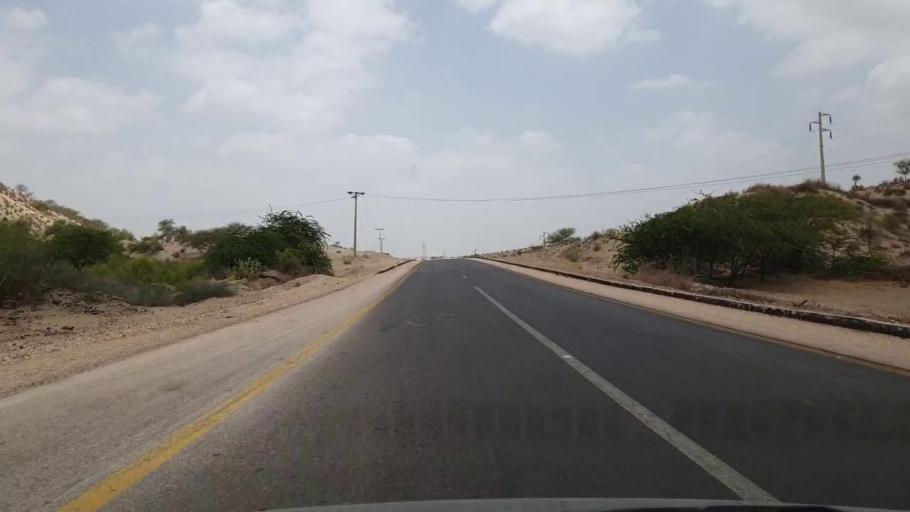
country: PK
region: Sindh
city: Naukot
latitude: 24.8352
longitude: 69.4708
